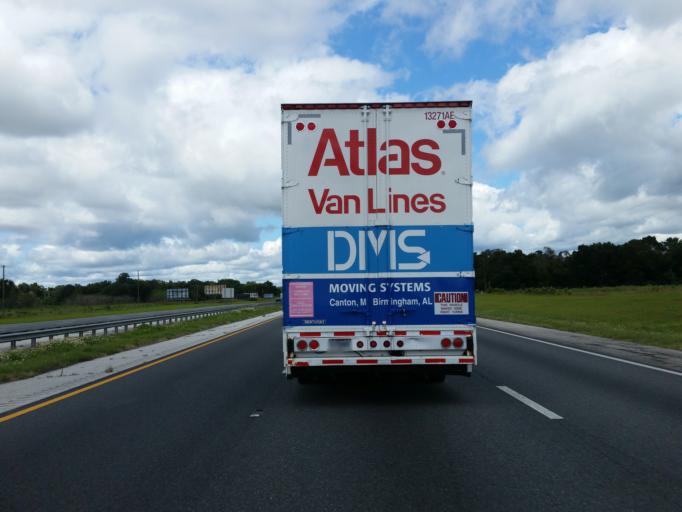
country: US
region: Florida
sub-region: Sumter County
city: Wildwood
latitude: 28.8883
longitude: -82.0967
